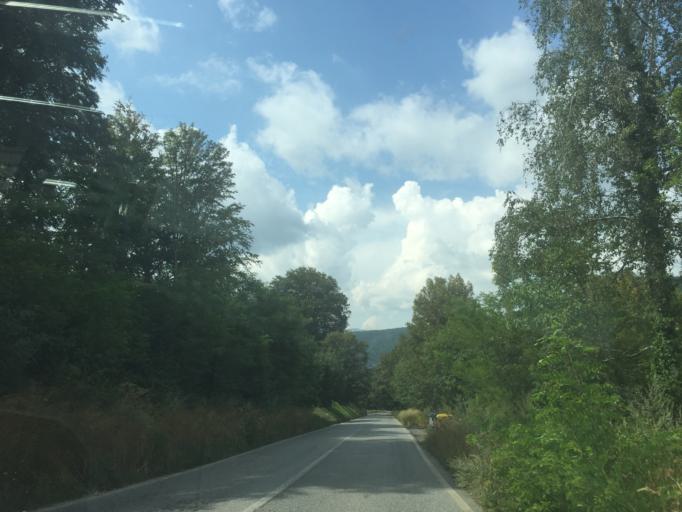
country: IT
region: Tuscany
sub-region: Provincia di Pistoia
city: San Marcello Pistoiese
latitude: 44.0445
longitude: 10.8159
